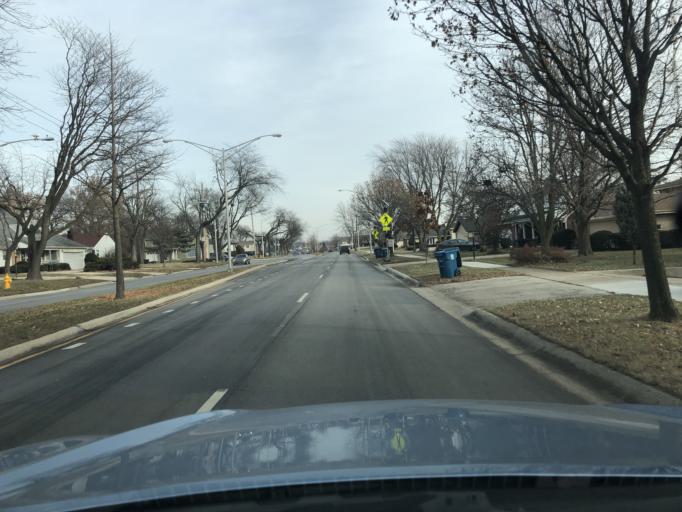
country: US
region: Illinois
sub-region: DuPage County
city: Addison
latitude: 41.9294
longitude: -88.0120
